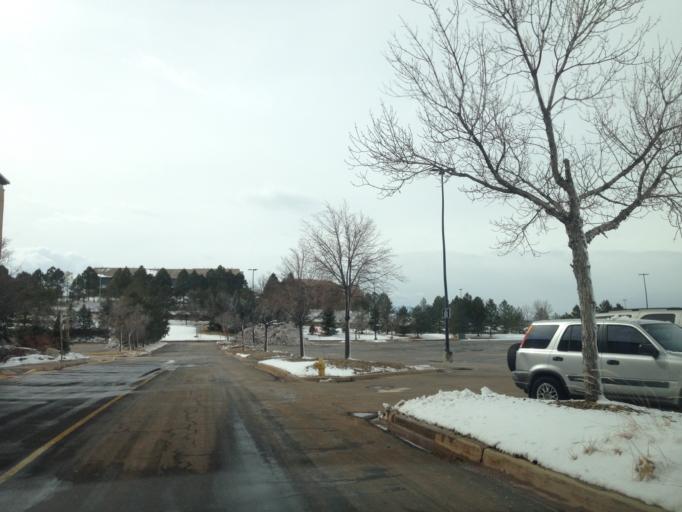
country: US
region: Colorado
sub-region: Boulder County
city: Superior
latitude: 39.9343
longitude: -105.1353
